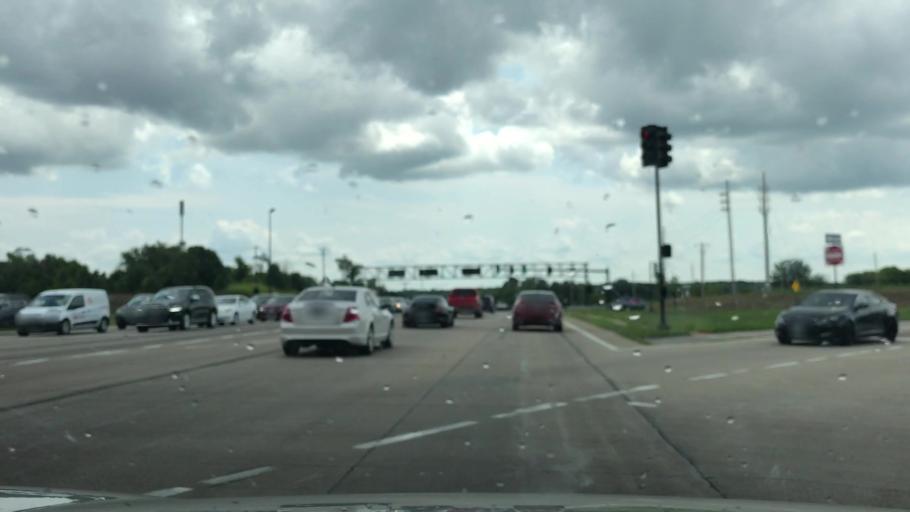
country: US
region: Missouri
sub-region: Saint Charles County
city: Dardenne Prairie
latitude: 38.7534
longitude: -90.7004
